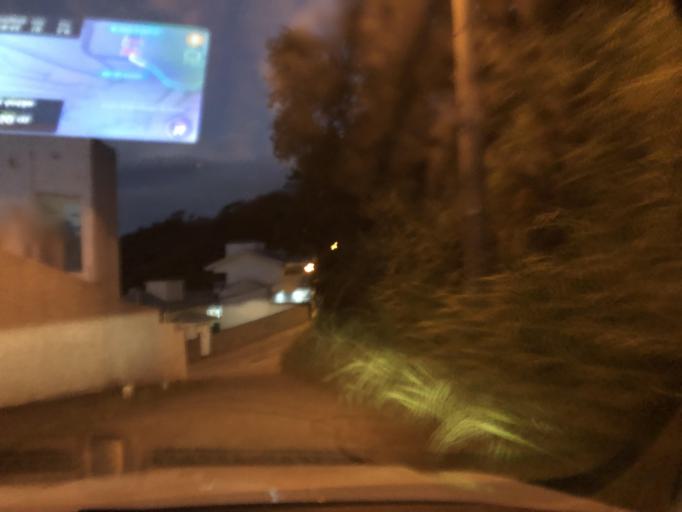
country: BR
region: Santa Catarina
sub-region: Florianopolis
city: Morro da Cruz
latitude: -27.5836
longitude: -48.5375
